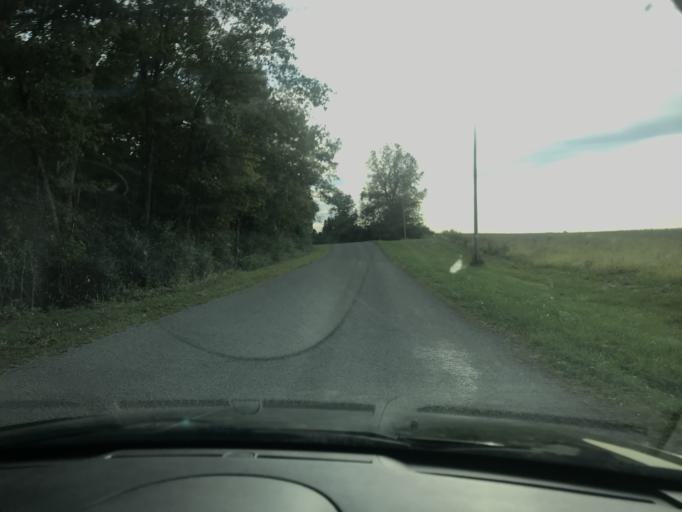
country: US
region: Ohio
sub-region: Champaign County
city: North Lewisburg
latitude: 40.2306
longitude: -83.6468
